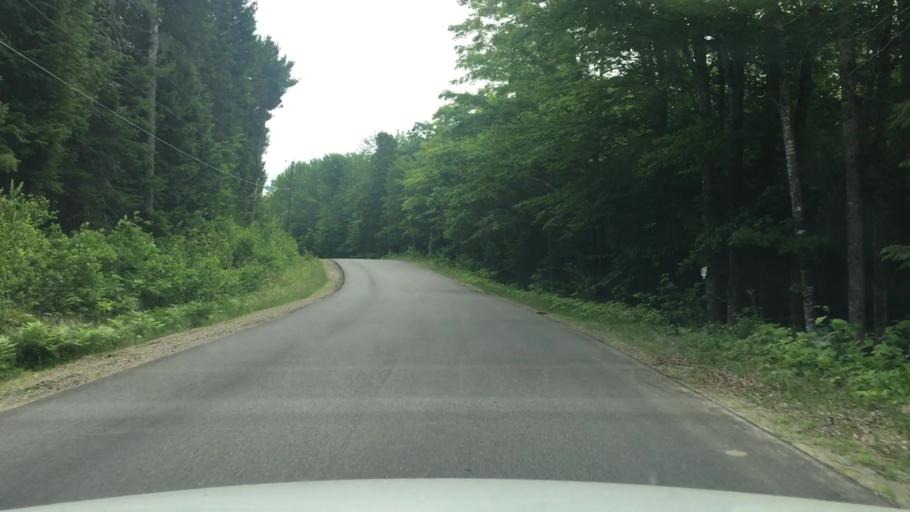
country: US
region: Maine
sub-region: Waldo County
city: Searsmont
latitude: 44.4493
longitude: -69.3078
